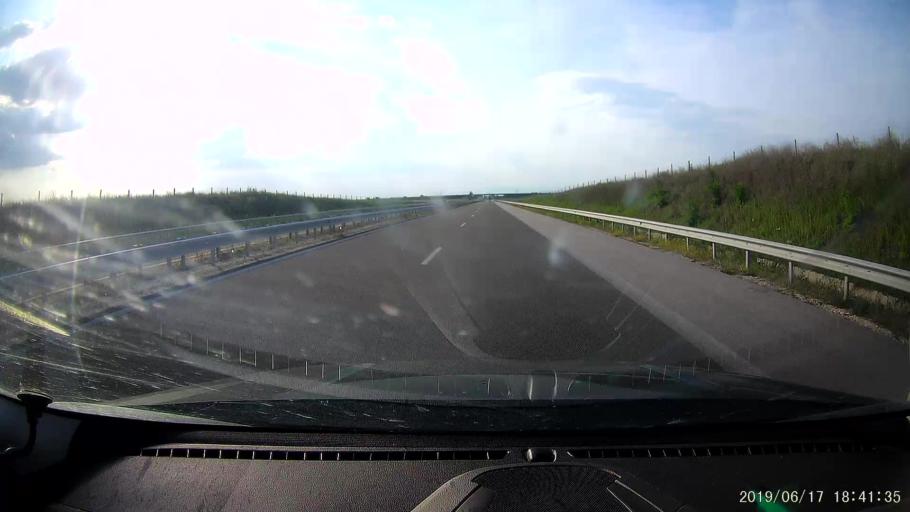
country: BG
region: Stara Zagora
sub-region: Obshtina Chirpan
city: Chirpan
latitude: 42.1752
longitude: 25.2530
